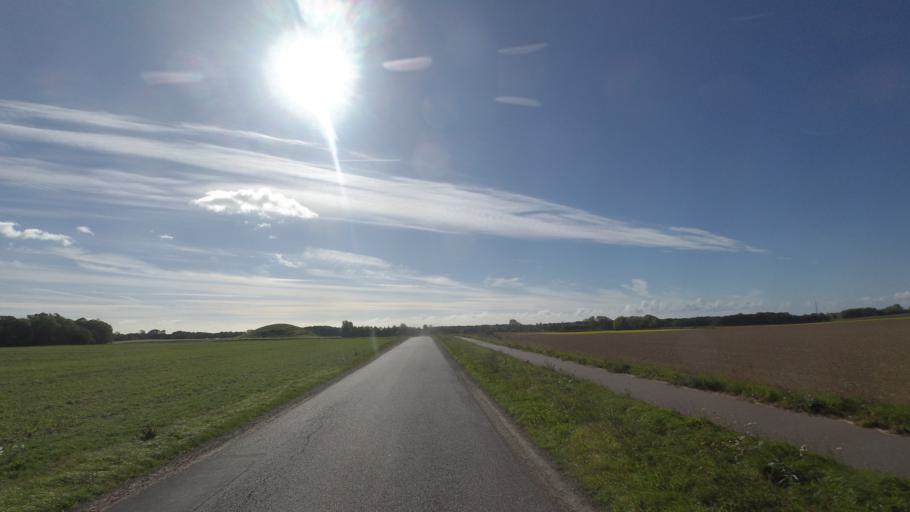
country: DK
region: Capital Region
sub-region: Bornholm Kommune
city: Akirkeby
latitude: 55.0184
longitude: 14.9927
